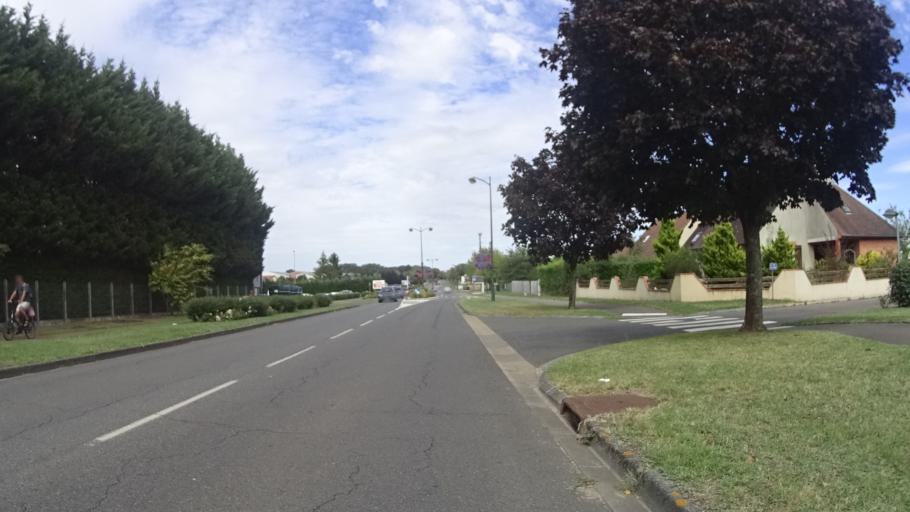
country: FR
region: Centre
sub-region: Departement du Loiret
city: Briare
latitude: 47.6516
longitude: 2.7363
